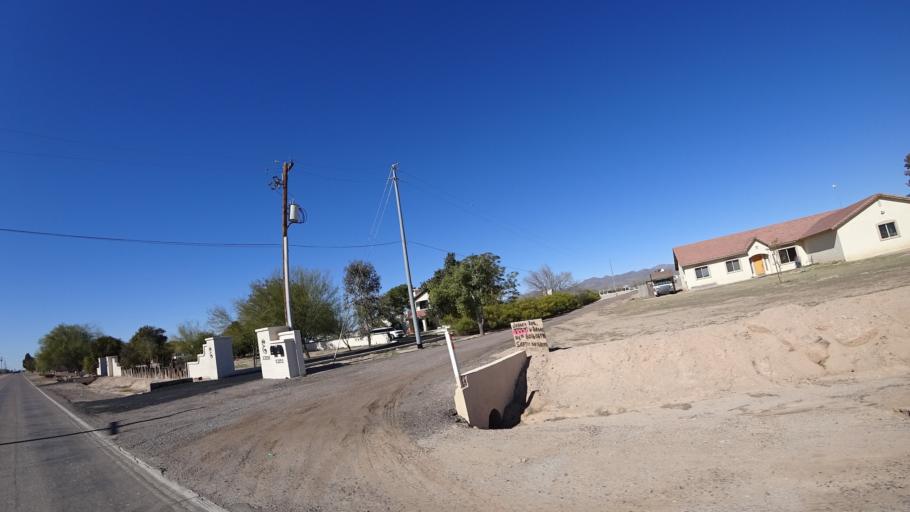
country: US
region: Arizona
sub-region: Maricopa County
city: Buckeye
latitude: 33.4067
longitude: -112.5512
